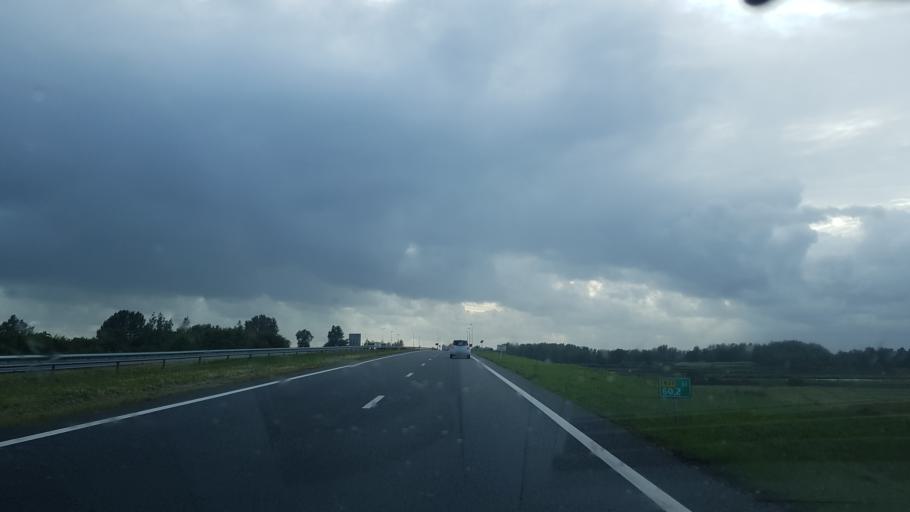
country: NL
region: Friesland
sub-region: Gemeente Tytsjerksteradiel
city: Garyp
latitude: 53.1640
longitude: 5.9375
